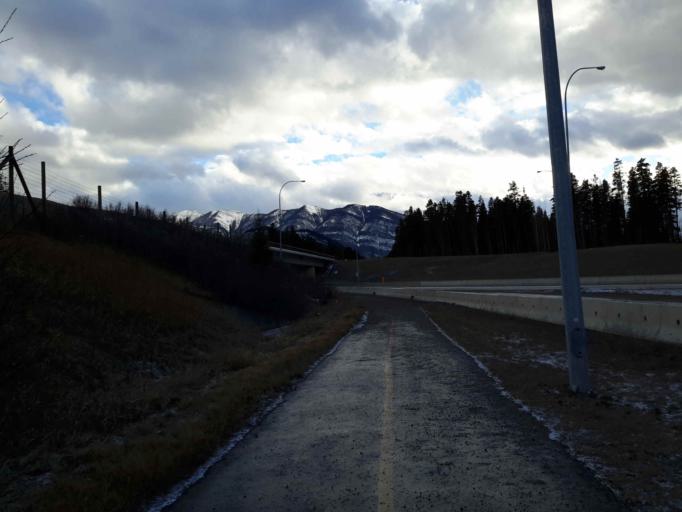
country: CA
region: Alberta
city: Banff
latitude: 51.2073
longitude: -115.5367
